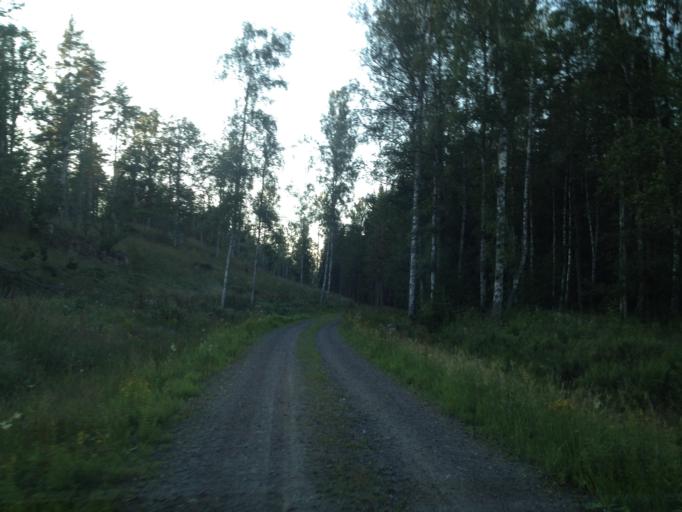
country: SE
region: Kalmar
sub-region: Vasterviks Kommun
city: Overum
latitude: 58.0145
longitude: 16.1196
